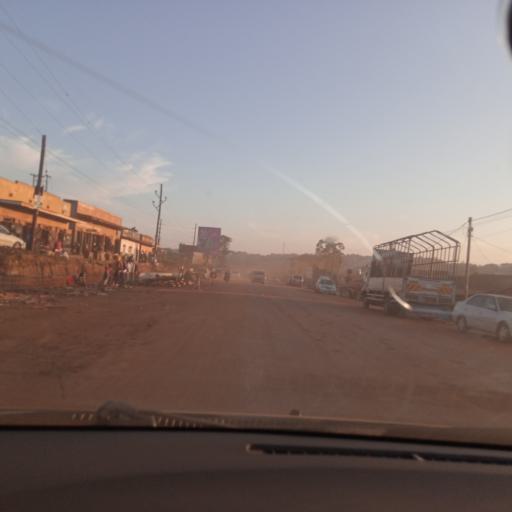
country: UG
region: Central Region
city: Masaka
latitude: -0.3236
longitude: 31.7549
